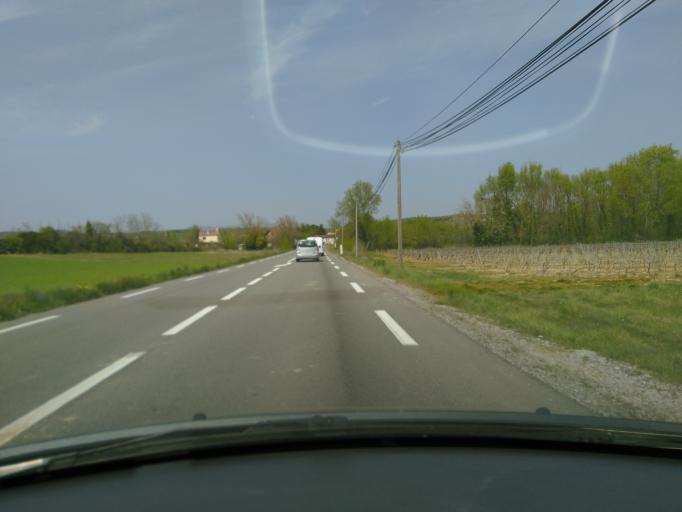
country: FR
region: Rhone-Alpes
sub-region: Departement de l'Ardeche
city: Saint-Sernin
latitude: 44.5318
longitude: 4.4178
